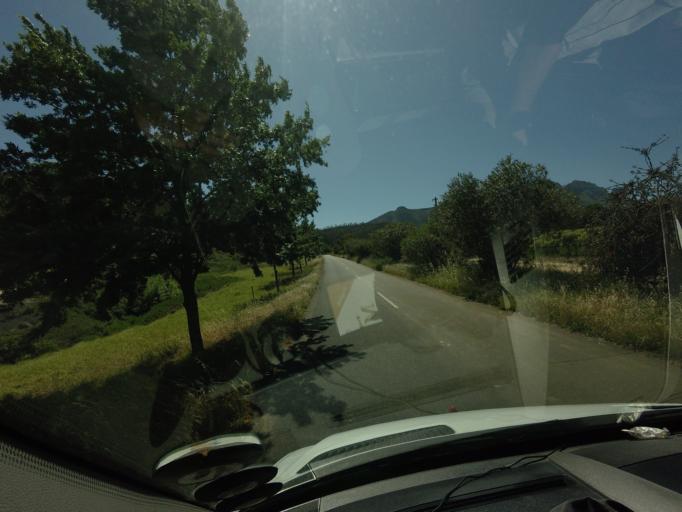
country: ZA
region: Western Cape
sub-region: Cape Winelands District Municipality
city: Stellenbosch
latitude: -33.8711
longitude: 18.8664
